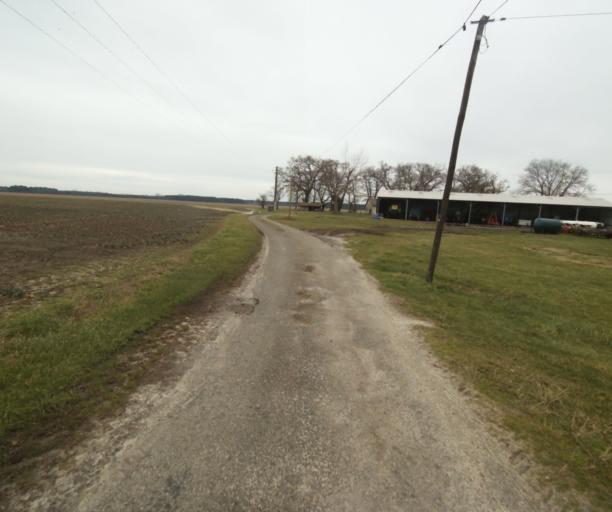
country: FR
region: Aquitaine
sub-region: Departement des Landes
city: Gabarret
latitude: 44.0167
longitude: -0.0135
